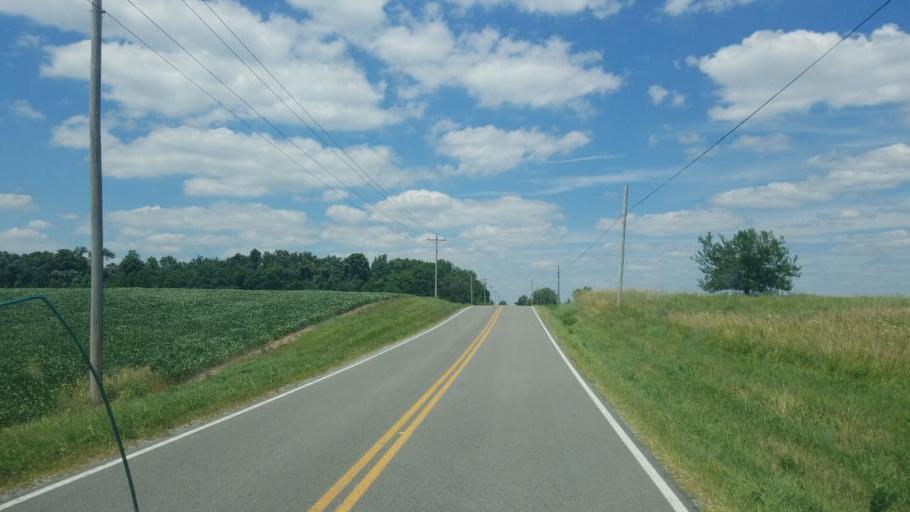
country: US
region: Ohio
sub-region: Williams County
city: Edgerton
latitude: 41.4187
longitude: -84.7101
